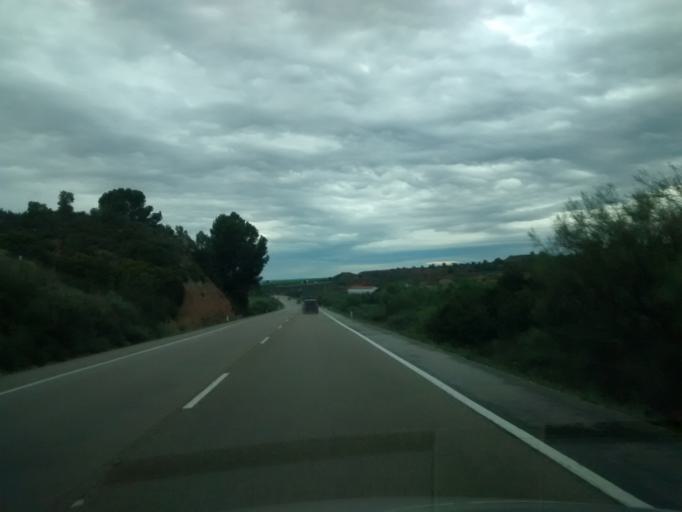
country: ES
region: Aragon
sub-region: Provincia de Zaragoza
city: Maella
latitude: 41.1684
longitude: 0.0737
